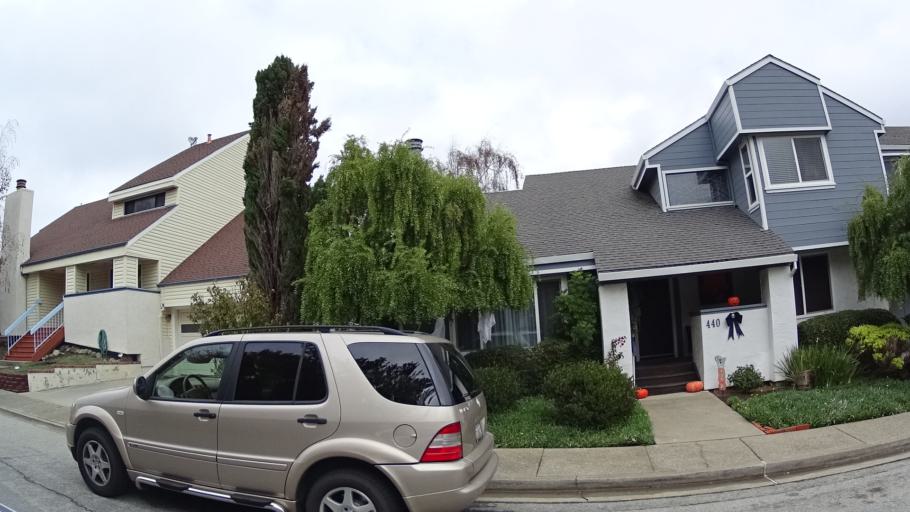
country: US
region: California
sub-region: San Mateo County
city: Millbrae
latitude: 37.6038
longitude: -122.4047
